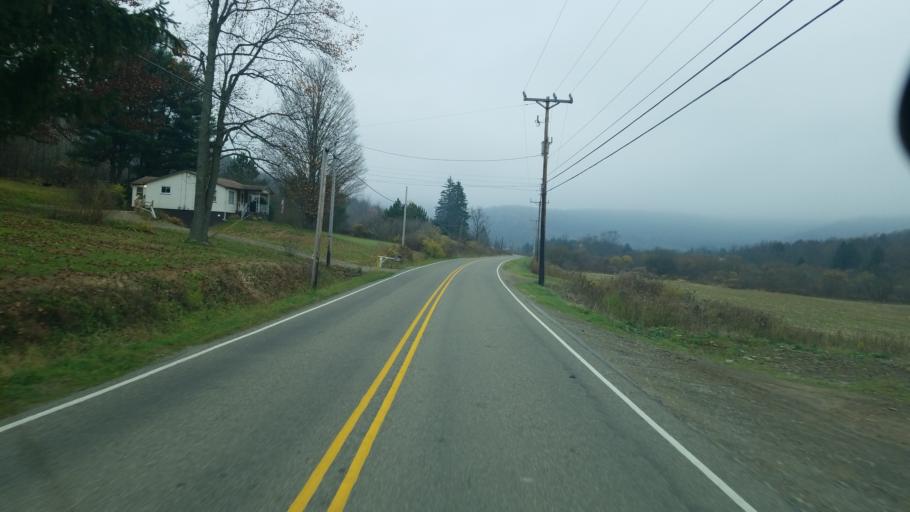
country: US
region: Pennsylvania
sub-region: McKean County
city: Smethport
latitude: 41.8681
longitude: -78.4762
